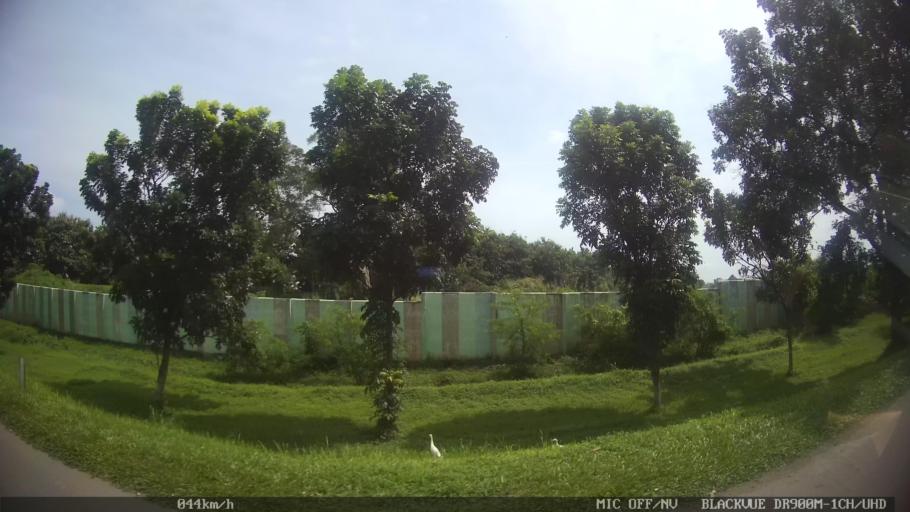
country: ID
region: North Sumatra
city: Medan
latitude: 3.6396
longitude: 98.7009
